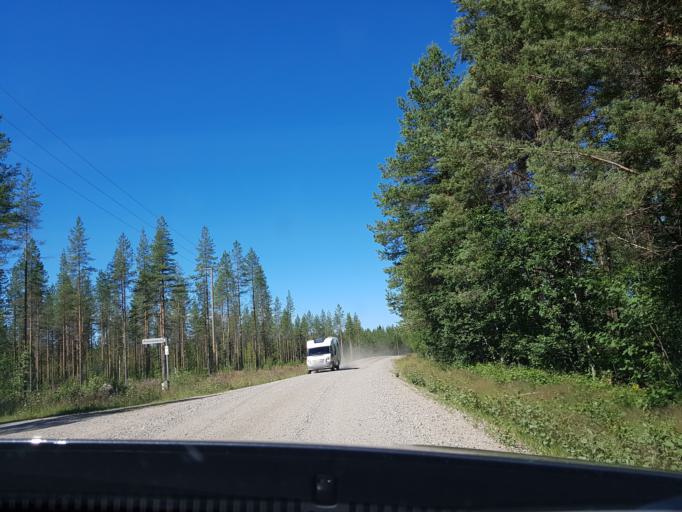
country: FI
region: Kainuu
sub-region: Kehys-Kainuu
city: Kuhmo
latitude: 64.1755
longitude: 29.6174
